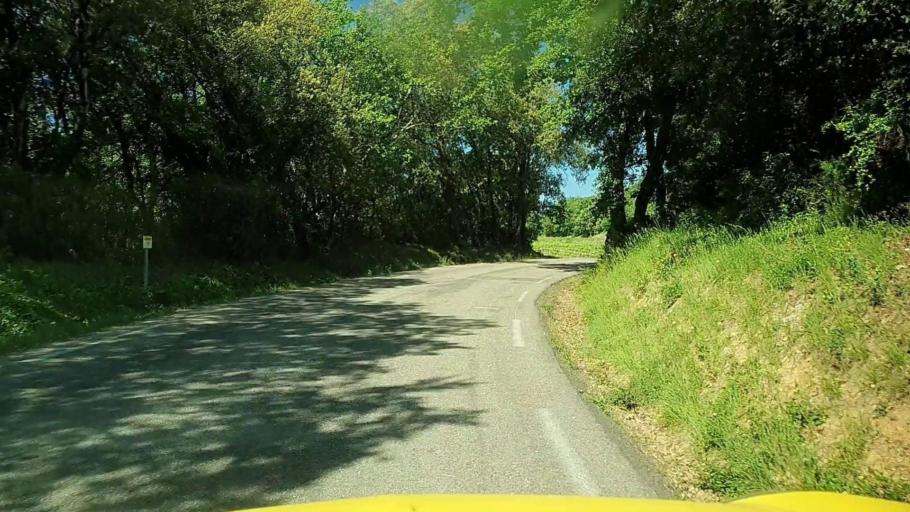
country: FR
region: Languedoc-Roussillon
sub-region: Departement du Gard
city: Blauzac
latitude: 43.9443
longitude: 4.3675
